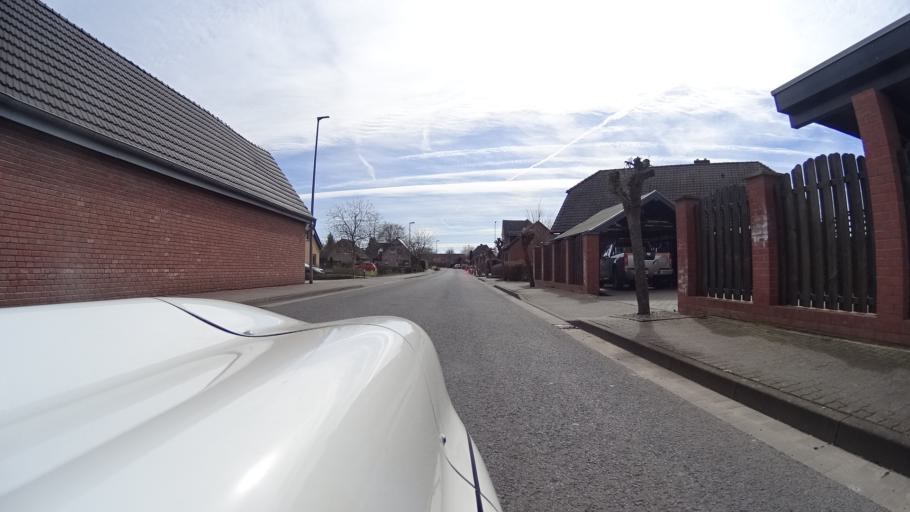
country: DE
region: North Rhine-Westphalia
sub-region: Regierungsbezirk Dusseldorf
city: Goch
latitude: 51.7074
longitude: 6.0727
